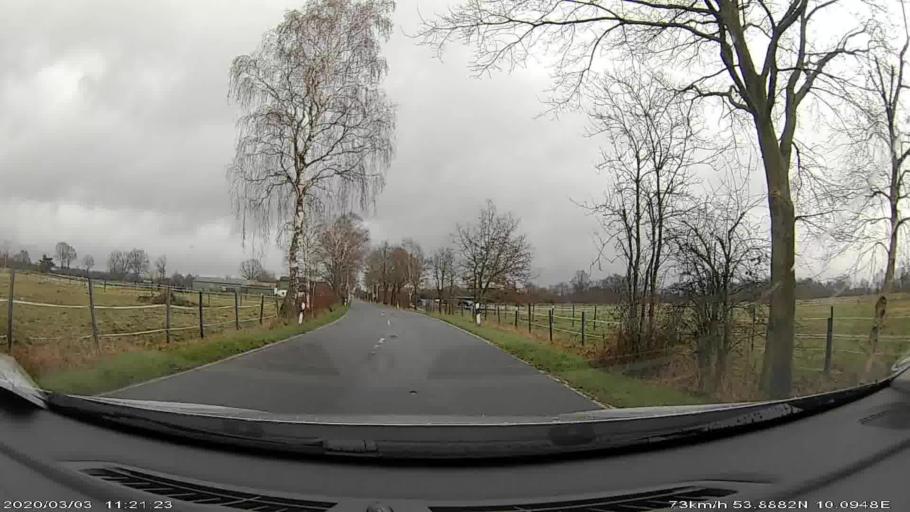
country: DE
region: Schleswig-Holstein
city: Hartenholm
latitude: 53.8884
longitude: 10.0997
